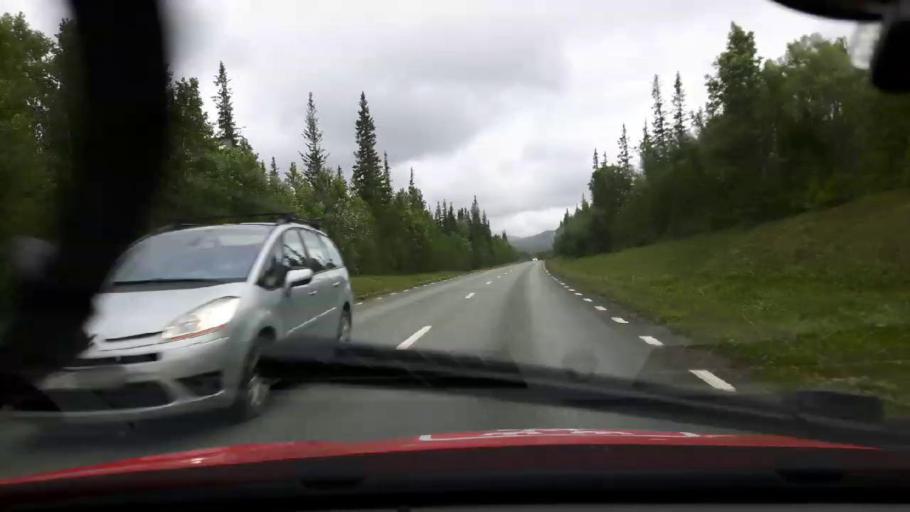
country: NO
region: Nord-Trondelag
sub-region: Meraker
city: Meraker
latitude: 63.2628
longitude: 12.1685
